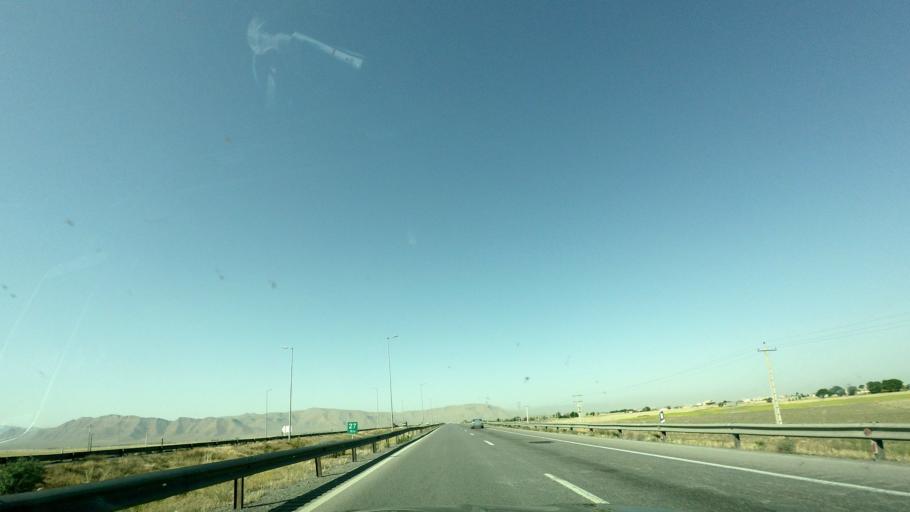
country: IR
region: Markazi
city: Ashtian
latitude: 34.1717
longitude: 50.0358
